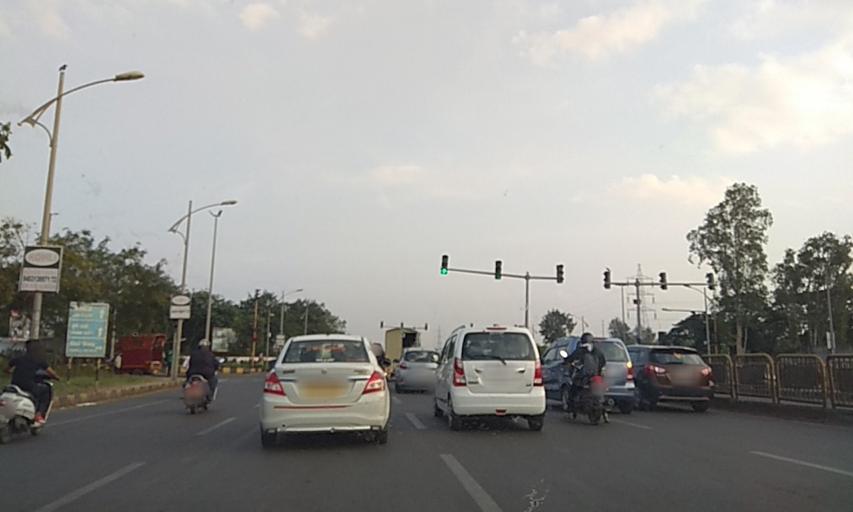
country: IN
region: Maharashtra
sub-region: Pune Division
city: Pimpri
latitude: 18.5827
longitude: 73.7972
